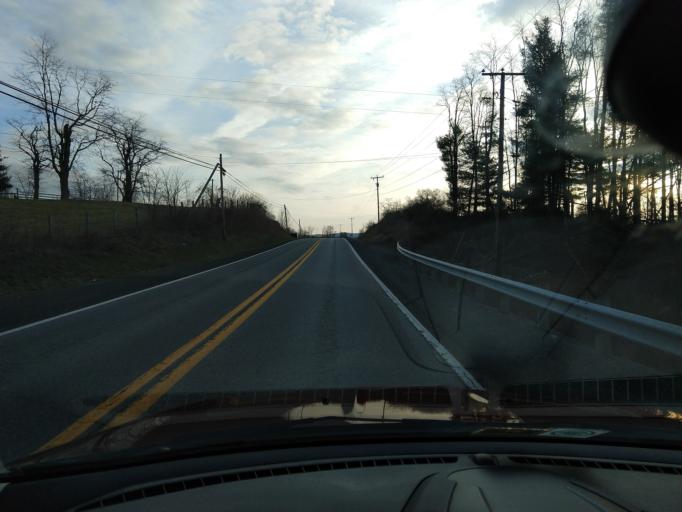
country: US
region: West Virginia
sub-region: Greenbrier County
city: Lewisburg
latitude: 37.9051
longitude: -80.3909
